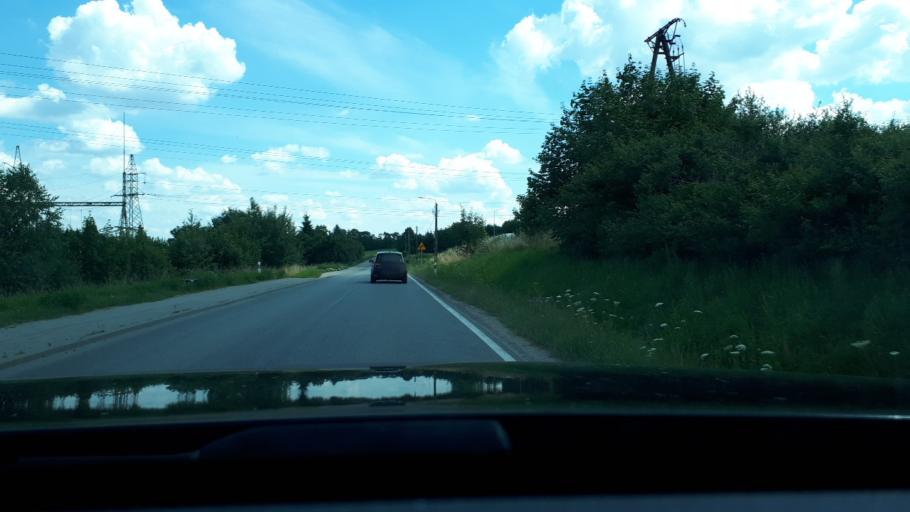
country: PL
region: Warmian-Masurian Voivodeship
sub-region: Powiat olsztynski
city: Olsztynek
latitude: 53.5830
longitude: 20.2996
